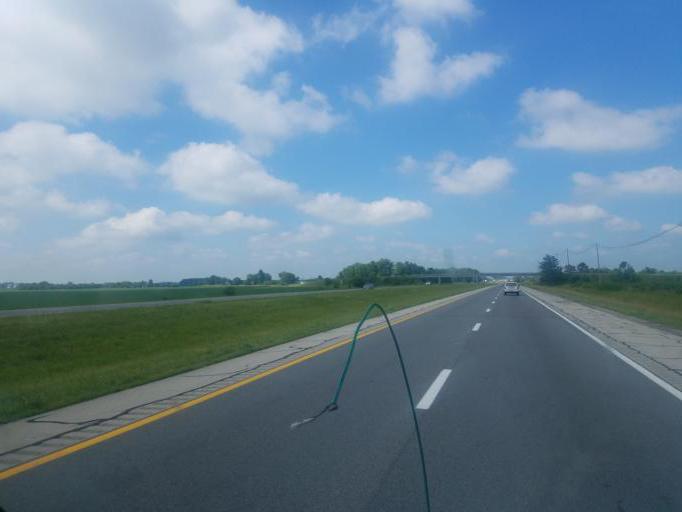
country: US
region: Ohio
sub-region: Fayette County
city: Jeffersonville
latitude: 39.6722
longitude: -83.5011
